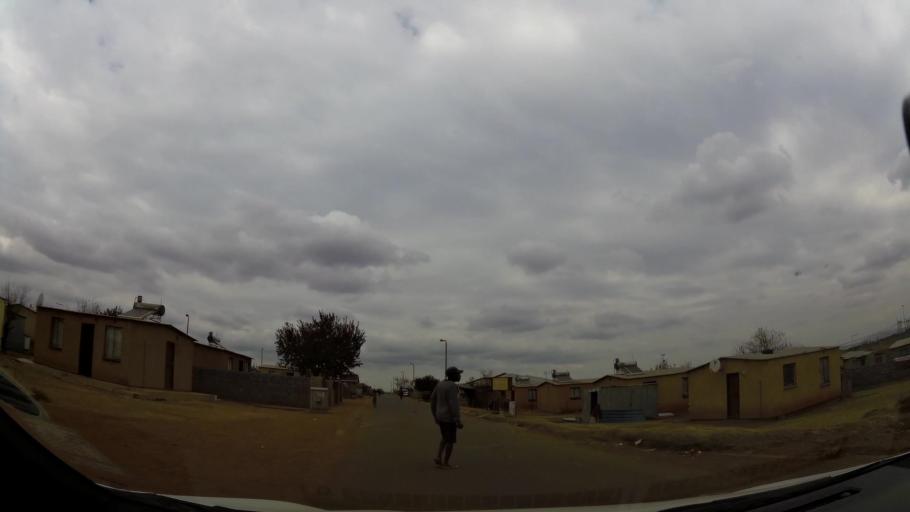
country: ZA
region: Gauteng
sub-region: Ekurhuleni Metropolitan Municipality
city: Germiston
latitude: -26.3764
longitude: 28.1173
